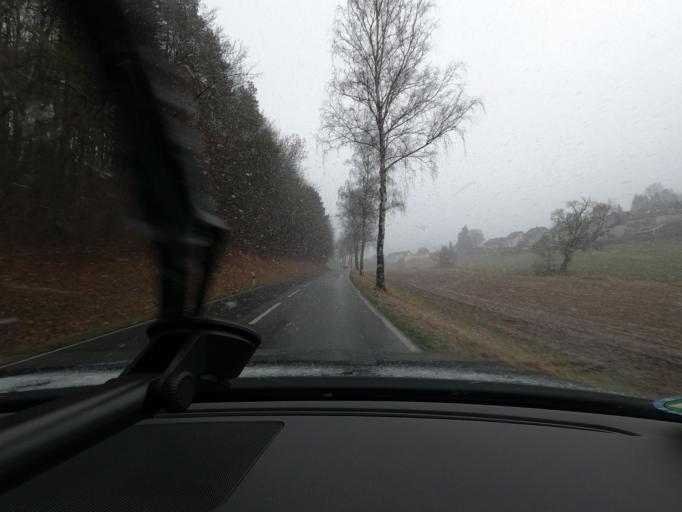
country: DE
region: North Rhine-Westphalia
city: Marsberg
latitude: 51.4994
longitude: 8.9077
